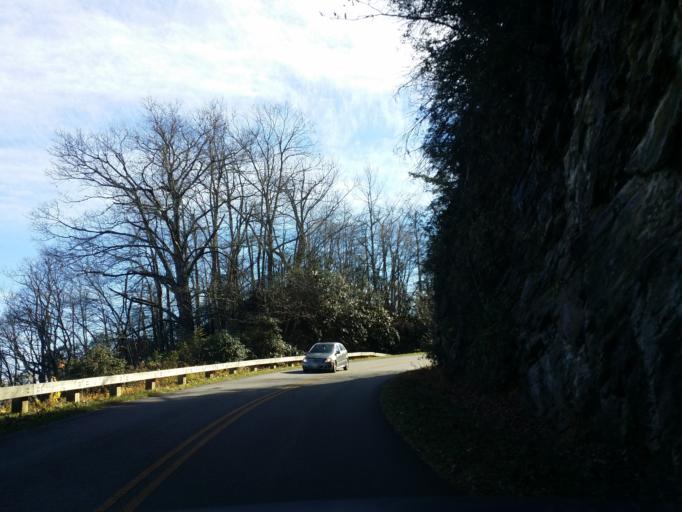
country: US
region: North Carolina
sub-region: Buncombe County
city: Black Mountain
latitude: 35.7435
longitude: -82.1884
